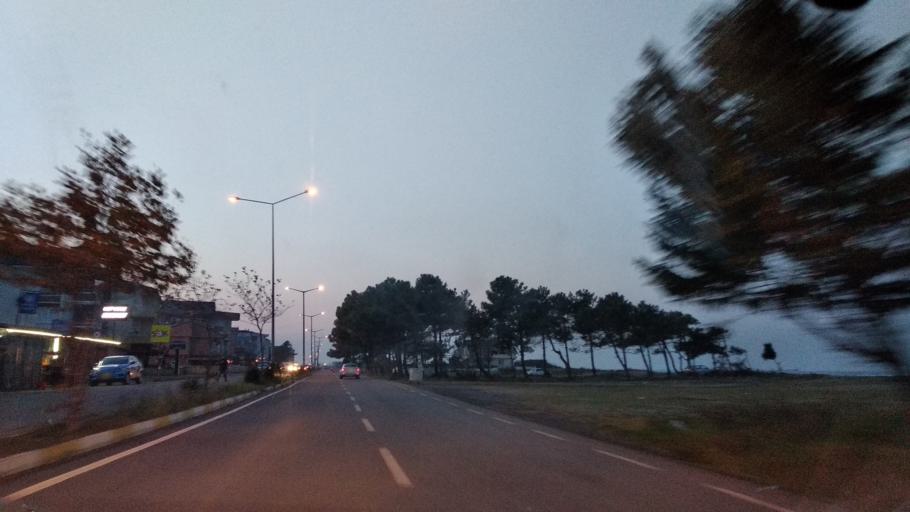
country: TR
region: Sakarya
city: Karasu
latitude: 41.0946
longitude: 30.7340
